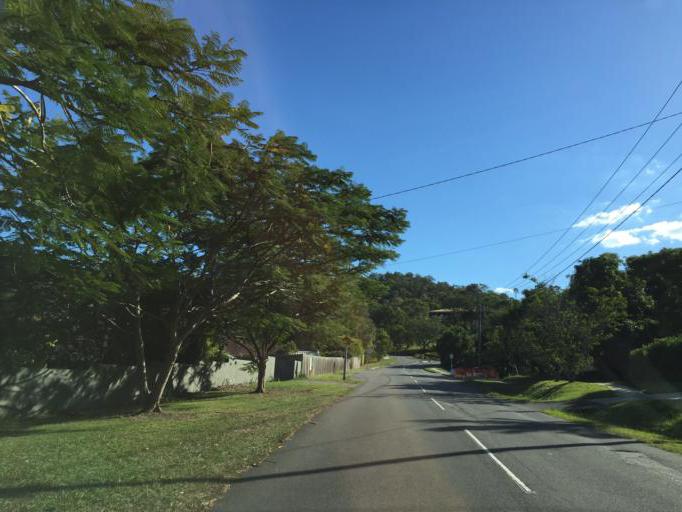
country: AU
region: Queensland
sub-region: Brisbane
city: Kenmore Hills
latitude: -27.4518
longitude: 152.9335
